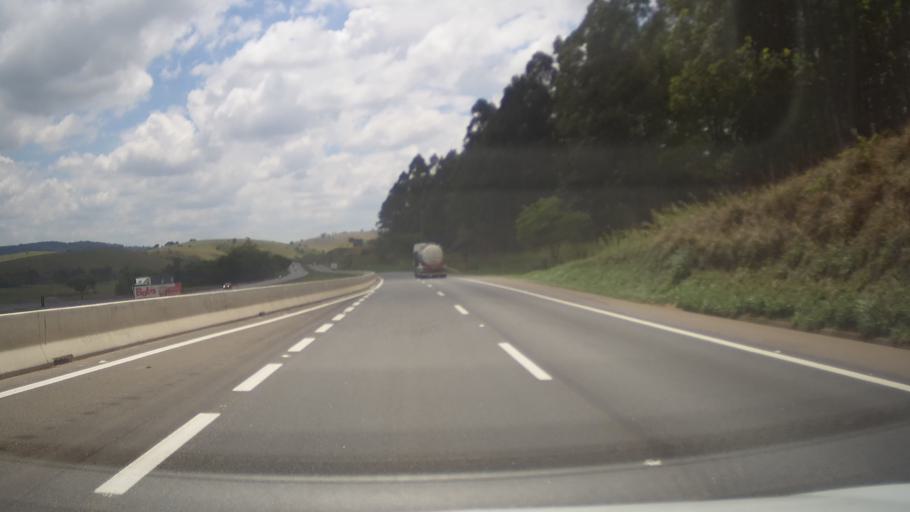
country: BR
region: Minas Gerais
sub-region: Campanha
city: Campanha
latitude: -21.7207
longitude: -45.3790
